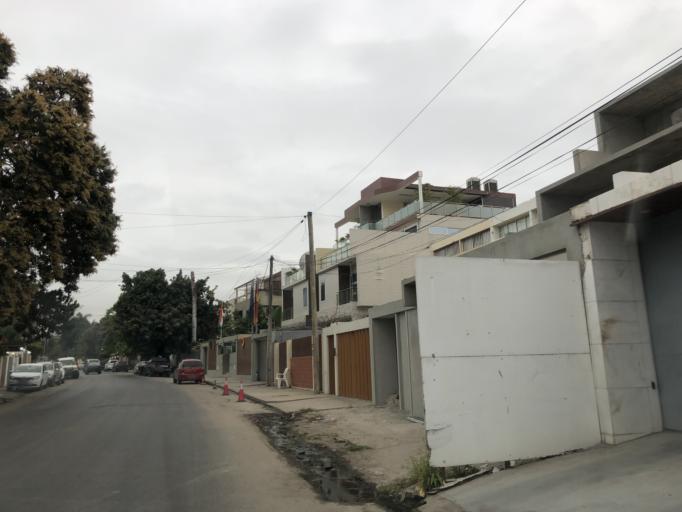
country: AO
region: Luanda
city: Luanda
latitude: -8.8319
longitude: 13.2325
